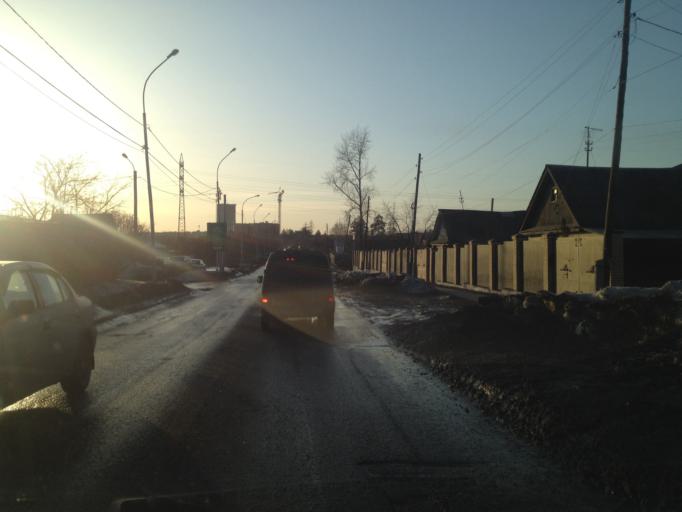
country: RU
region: Sverdlovsk
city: Sovkhoznyy
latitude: 56.7638
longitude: 60.5636
